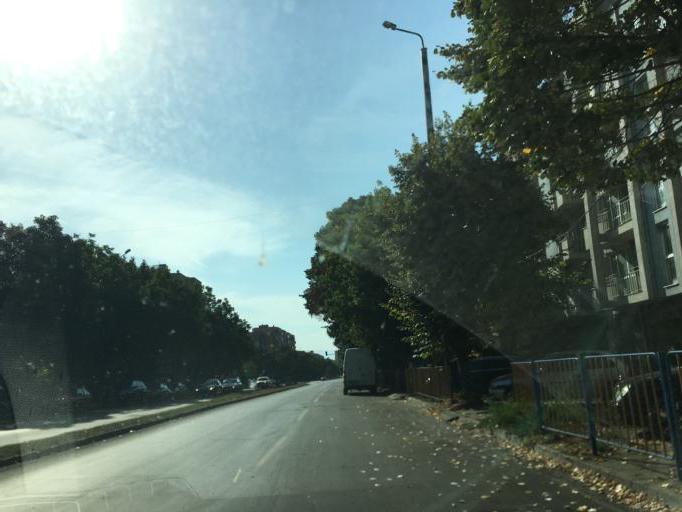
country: BG
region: Pazardzhik
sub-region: Obshtina Pazardzhik
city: Pazardzhik
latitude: 42.2065
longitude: 24.3287
